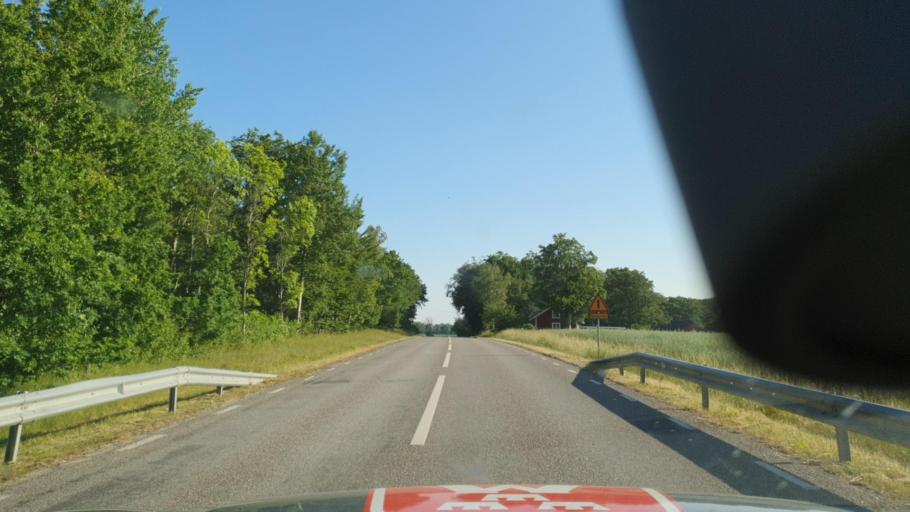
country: SE
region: Kalmar
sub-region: Kalmar Kommun
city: Ljungbyholm
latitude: 56.5133
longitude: 16.1528
